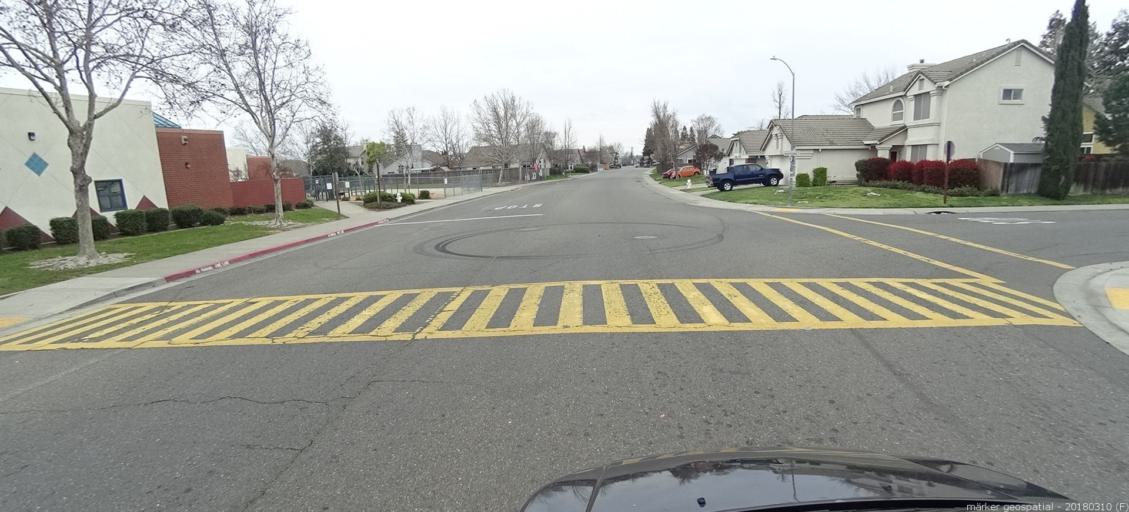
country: US
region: California
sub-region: Sacramento County
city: Vineyard
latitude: 38.4616
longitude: -121.3640
